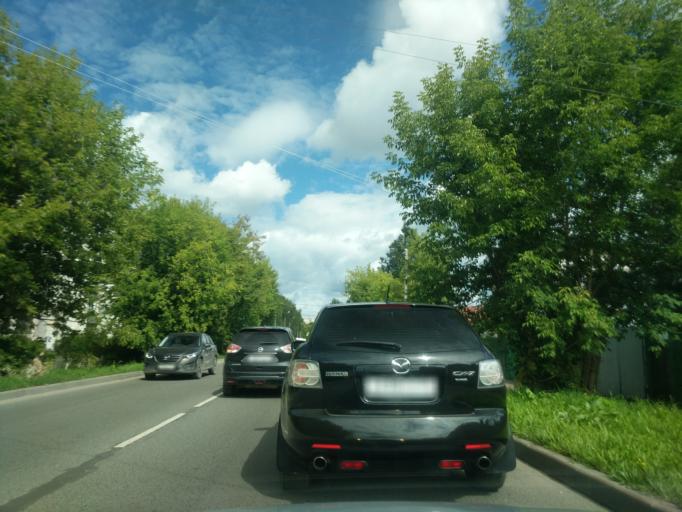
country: RU
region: Kostroma
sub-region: Kostromskoy Rayon
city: Kostroma
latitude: 57.7773
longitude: 40.9547
